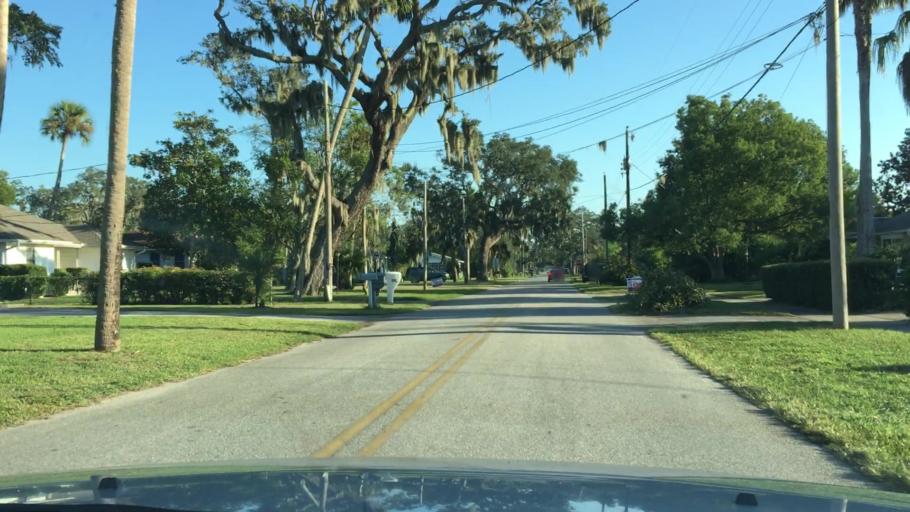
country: US
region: Florida
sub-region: Volusia County
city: Holly Hill
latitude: 29.2412
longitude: -81.0367
